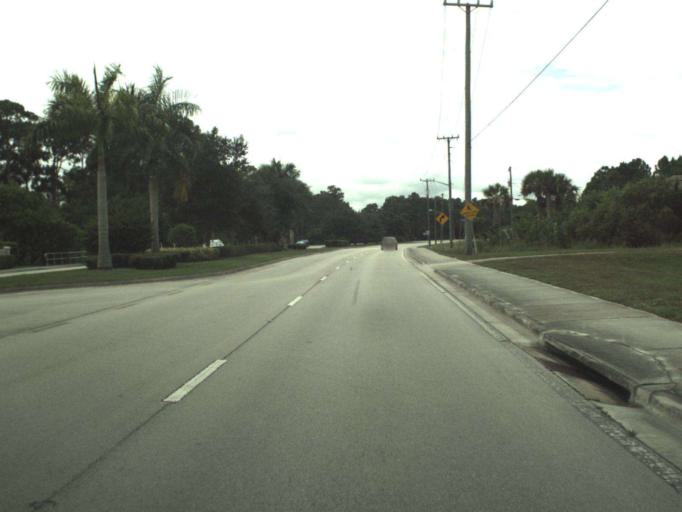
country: US
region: Florida
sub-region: Saint Lucie County
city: White City
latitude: 27.3675
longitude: -80.3504
